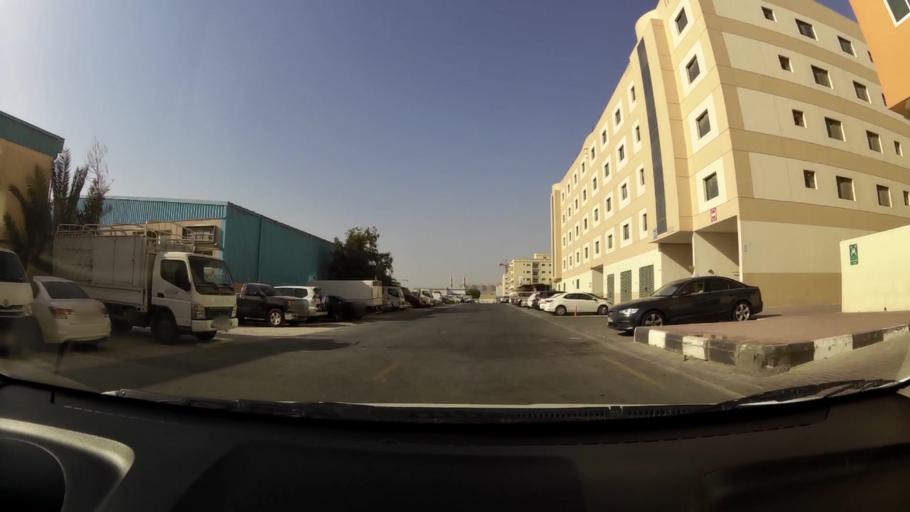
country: AE
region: Ash Shariqah
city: Sharjah
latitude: 25.2796
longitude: 55.3848
